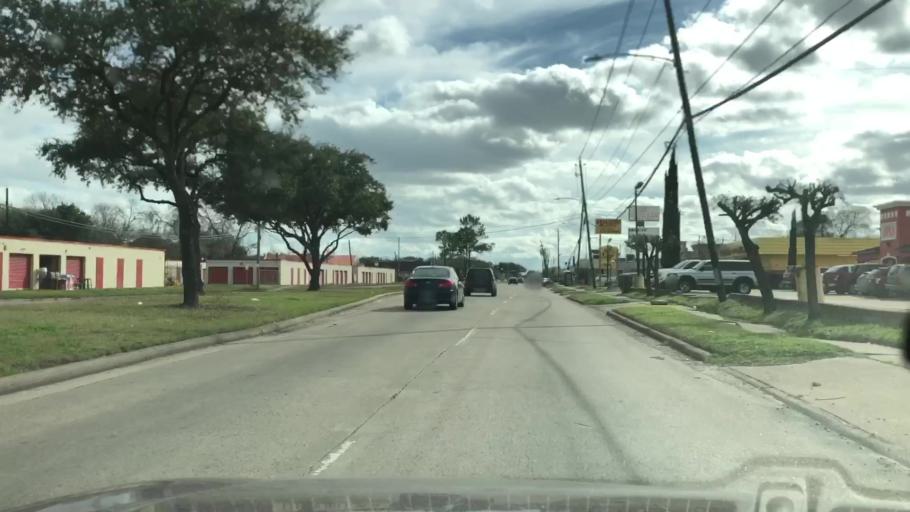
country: US
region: Texas
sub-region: Fort Bend County
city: Missouri City
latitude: 29.6182
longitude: -95.4651
